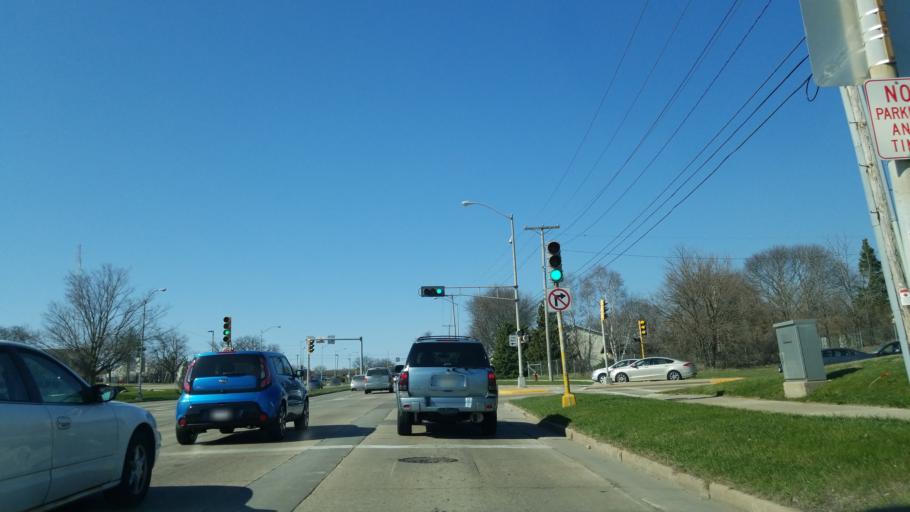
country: US
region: Wisconsin
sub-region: Dane County
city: Shorewood Hills
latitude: 43.0470
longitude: -89.4734
